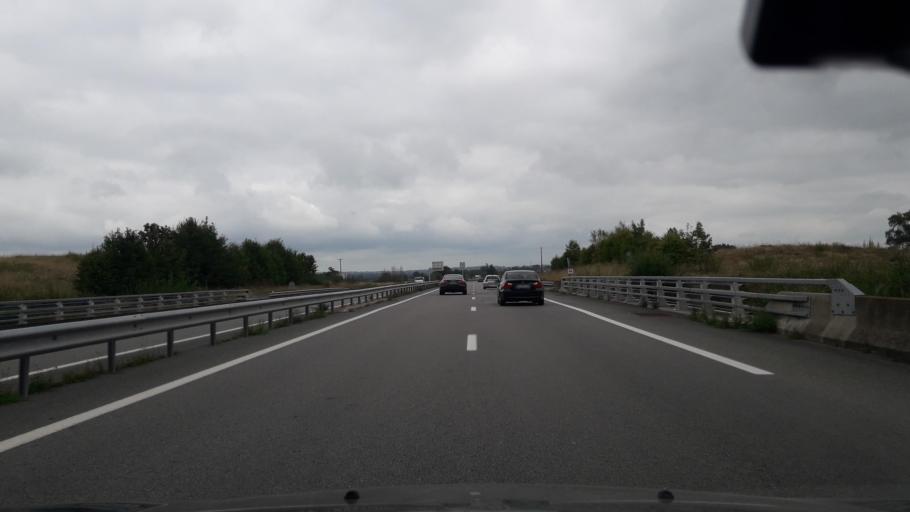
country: FR
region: Limousin
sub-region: Departement de la Creuse
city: Chambon-sur-Voueize
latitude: 46.2581
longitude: 2.3606
